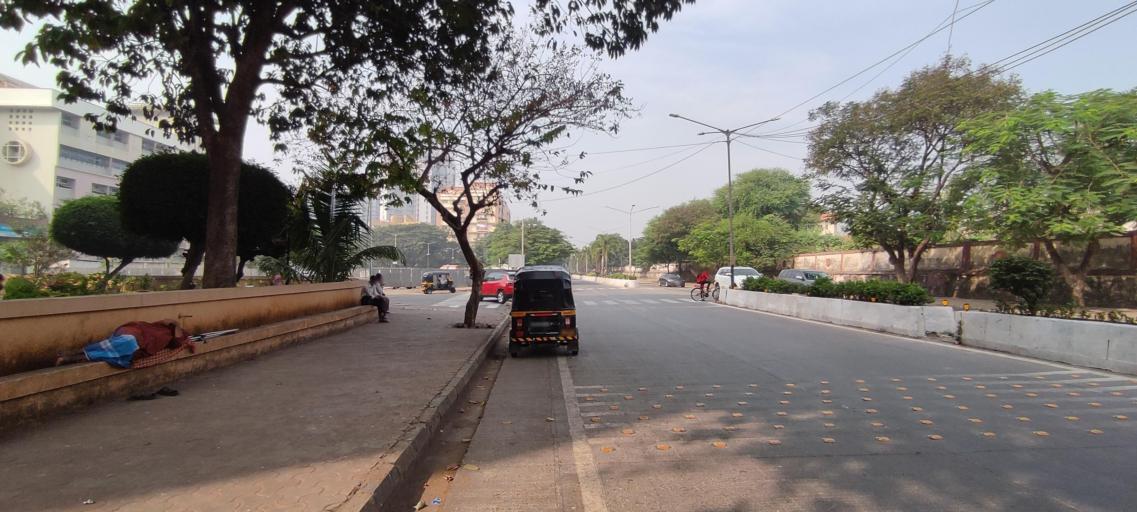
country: IN
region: Maharashtra
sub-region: Mumbai Suburban
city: Mumbai
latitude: 19.0659
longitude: 72.8598
